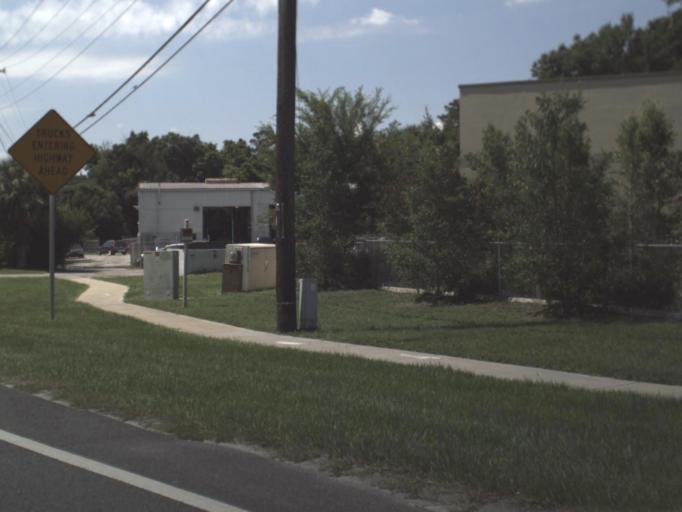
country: US
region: Florida
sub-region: Alachua County
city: Gainesville
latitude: 29.6353
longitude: -82.3271
